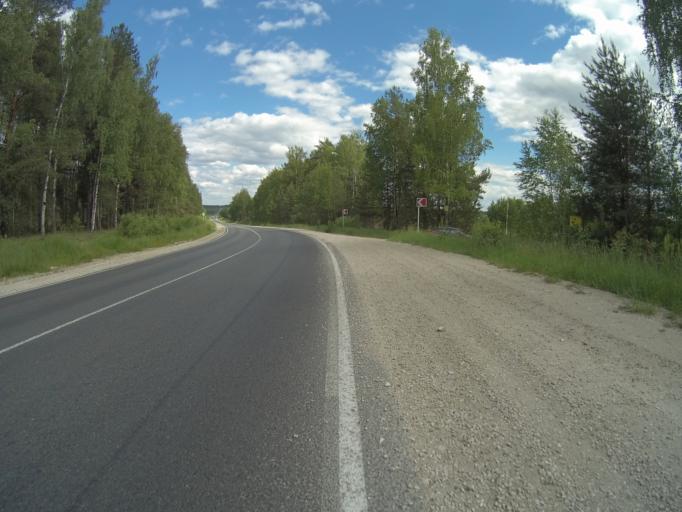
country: RU
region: Vladimir
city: Sudogda
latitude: 55.9839
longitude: 40.7008
